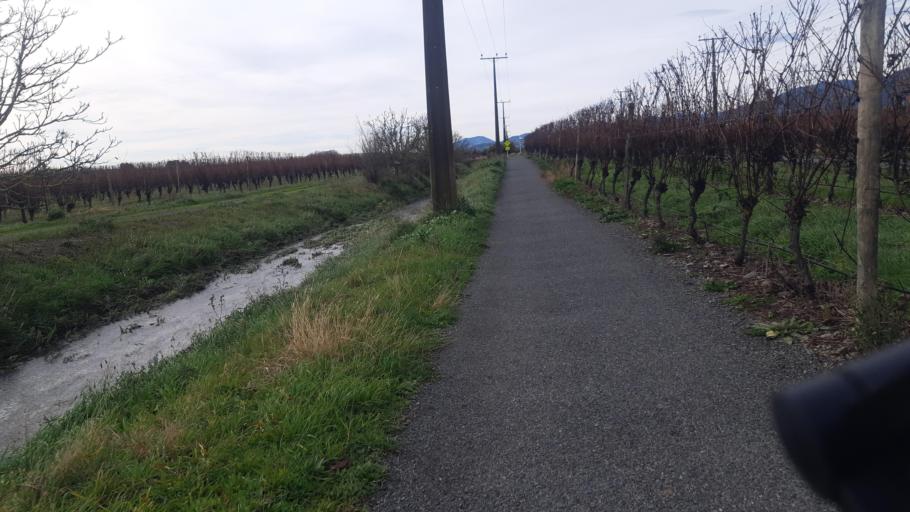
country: NZ
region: Tasman
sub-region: Tasman District
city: Richmond
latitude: -41.3480
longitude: 173.1595
